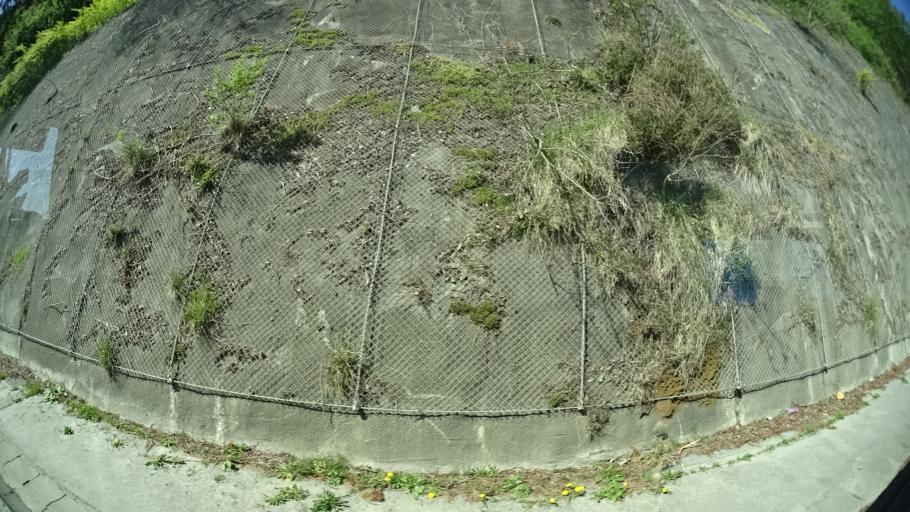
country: JP
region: Iwate
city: Ofunato
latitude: 39.0006
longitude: 141.6213
